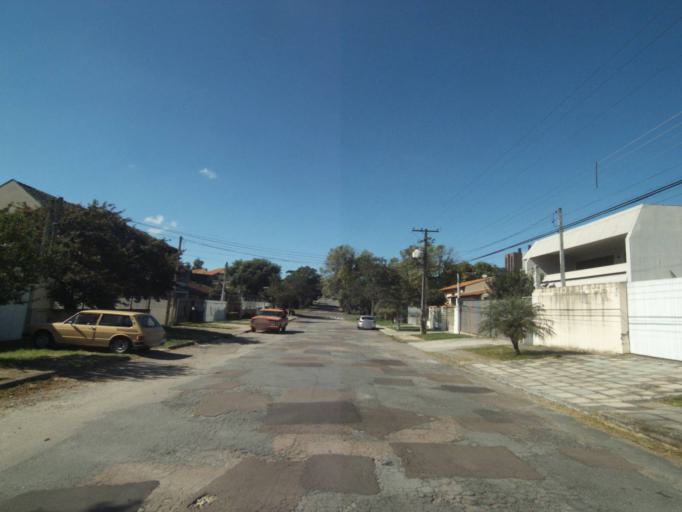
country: BR
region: Parana
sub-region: Pinhais
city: Pinhais
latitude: -25.4391
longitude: -49.2299
